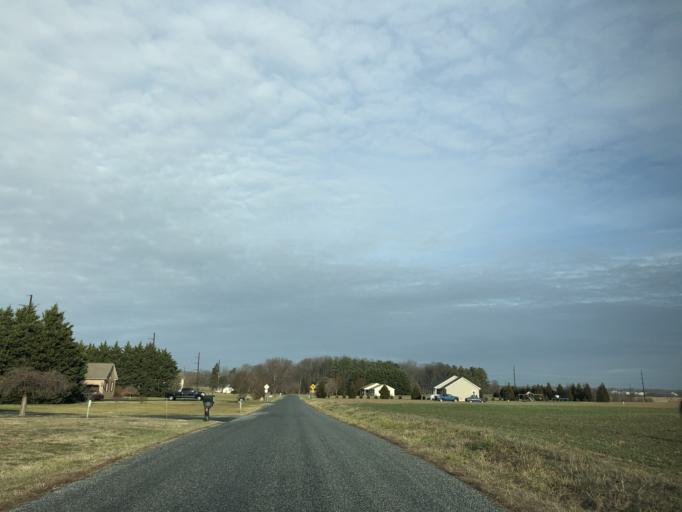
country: US
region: Delaware
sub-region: New Castle County
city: Townsend
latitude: 39.4502
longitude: -75.6314
